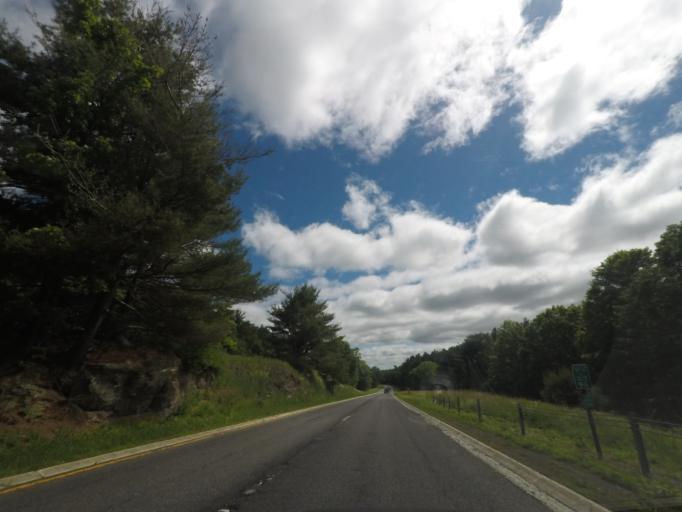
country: US
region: New York
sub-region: Columbia County
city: Chatham
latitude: 42.3084
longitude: -73.5796
